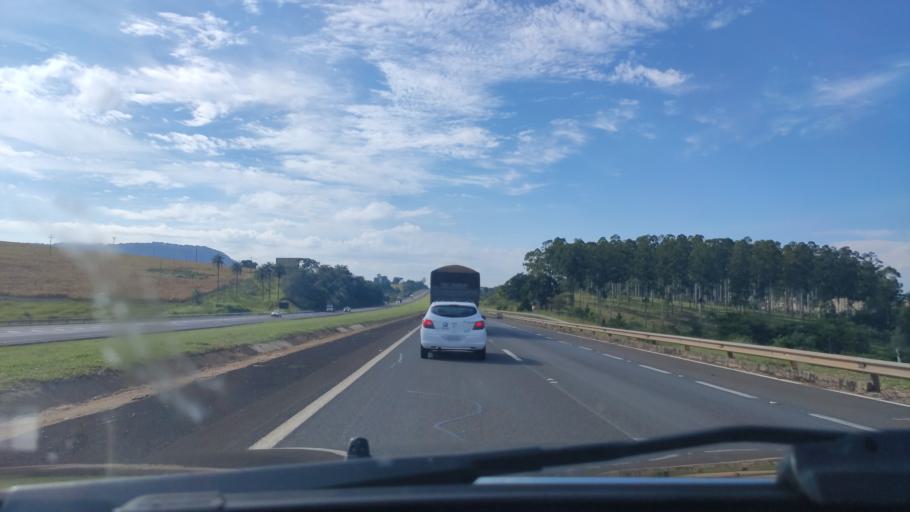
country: BR
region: Sao Paulo
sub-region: Itatinga
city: Itatinga
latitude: -23.1491
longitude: -48.3968
